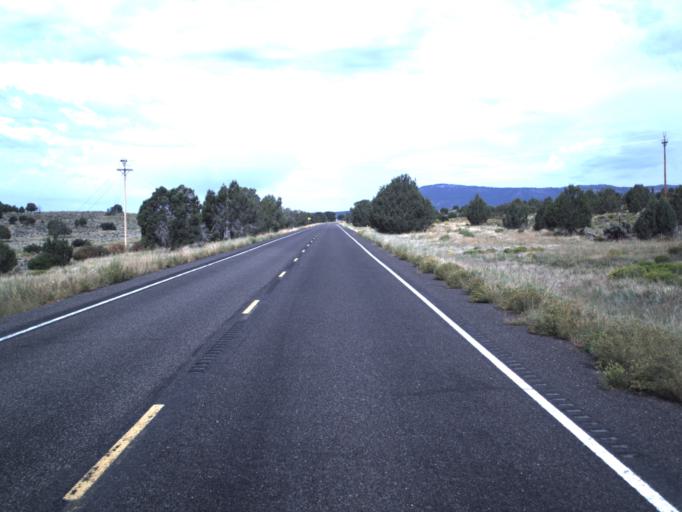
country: US
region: Utah
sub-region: Kane County
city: Kanab
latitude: 37.2242
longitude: -112.7195
